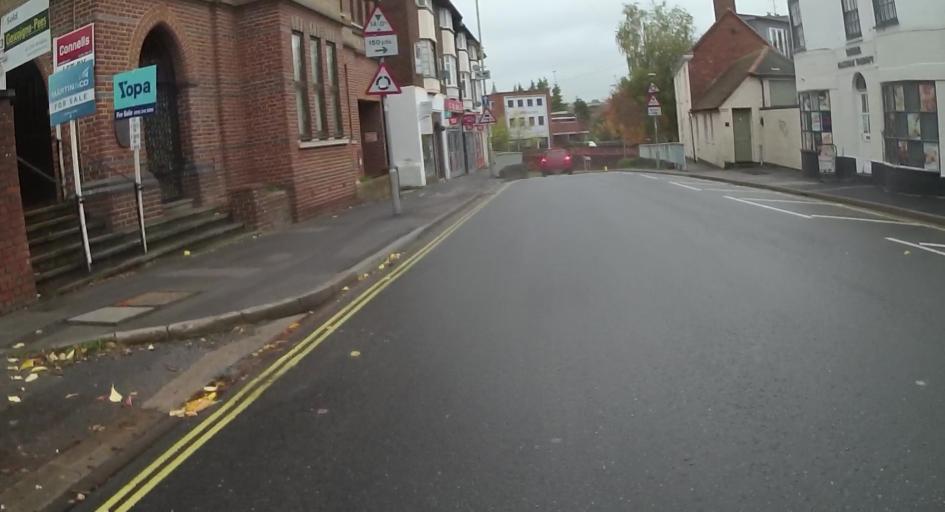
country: GB
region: England
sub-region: Hampshire
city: Basingstoke
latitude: 51.2631
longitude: -1.0890
